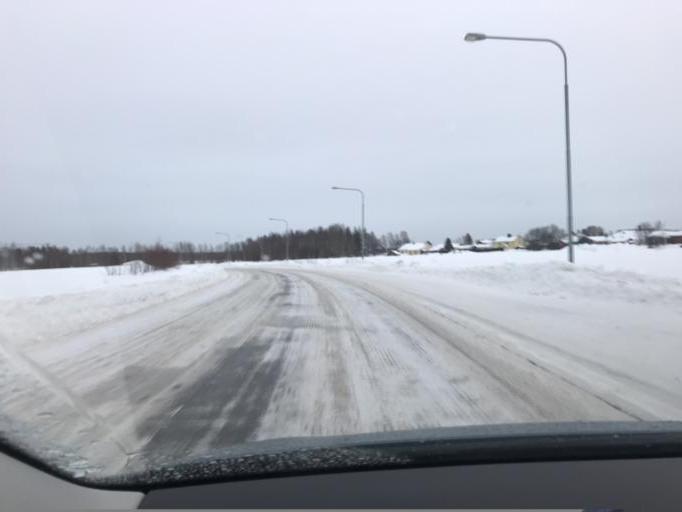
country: SE
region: Norrbotten
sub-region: Lulea Kommun
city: Sodra Sunderbyn
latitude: 65.6648
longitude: 21.9313
